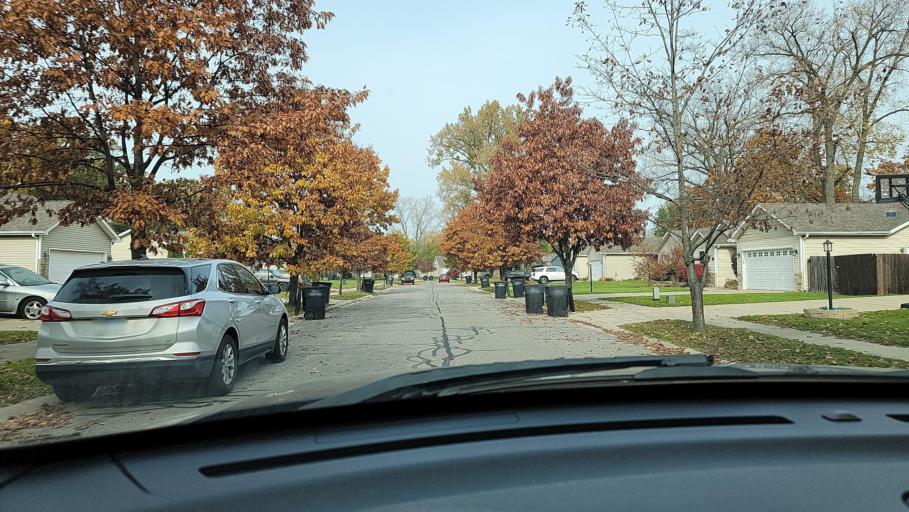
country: US
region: Indiana
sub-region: Porter County
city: Portage
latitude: 41.5891
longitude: -87.1691
